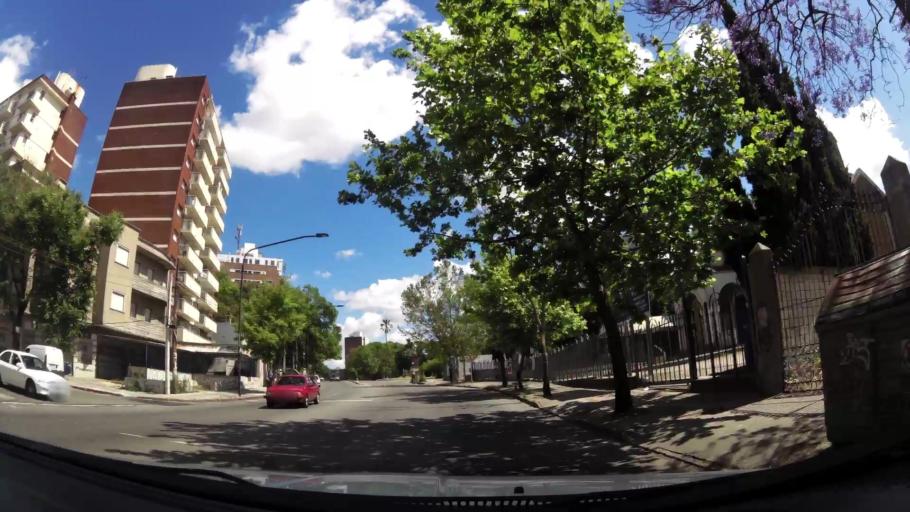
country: UY
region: Montevideo
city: Montevideo
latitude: -34.8784
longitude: -56.1963
